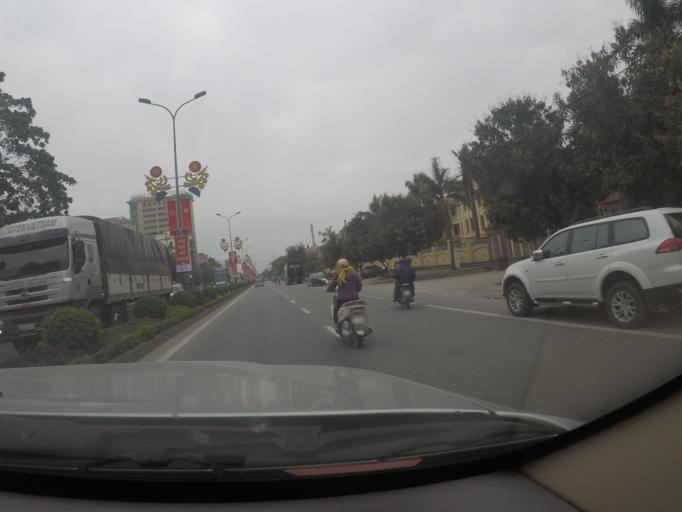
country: VN
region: Nghe An
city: Dien Chau
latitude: 18.9804
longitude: 105.6007
